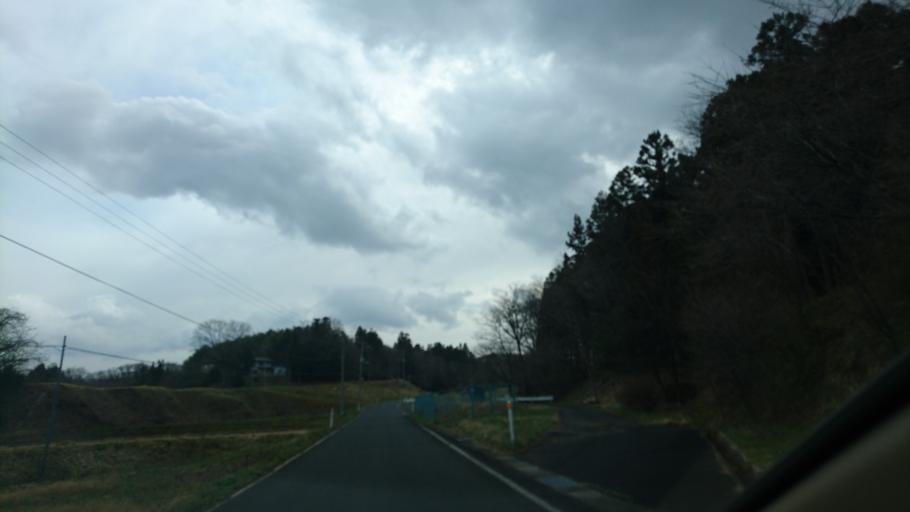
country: JP
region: Iwate
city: Ichinoseki
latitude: 38.8855
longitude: 141.1677
